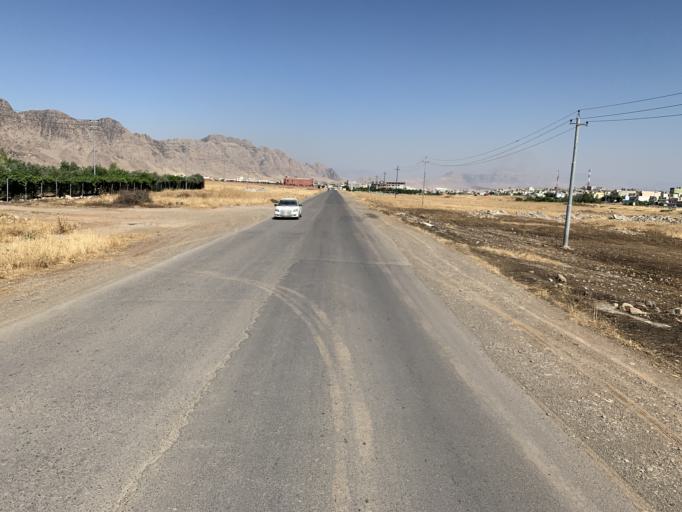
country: IQ
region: As Sulaymaniyah
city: Raniye
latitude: 36.2637
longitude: 44.8475
